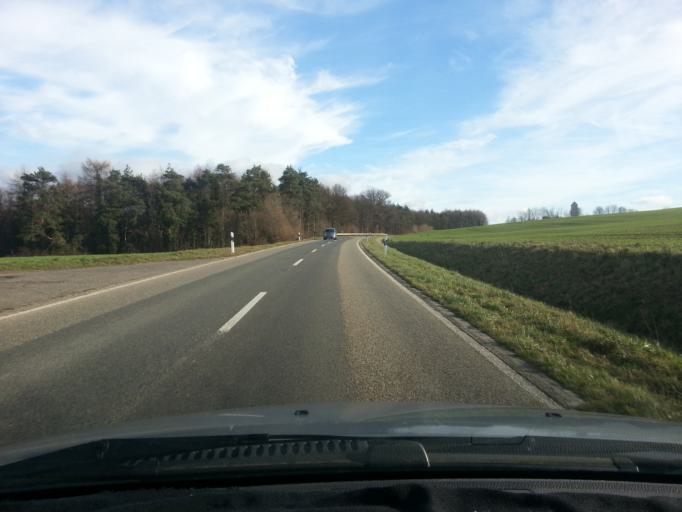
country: DE
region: Baden-Wuerttemberg
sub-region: Karlsruhe Region
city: Ostringen
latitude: 49.2056
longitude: 8.7512
